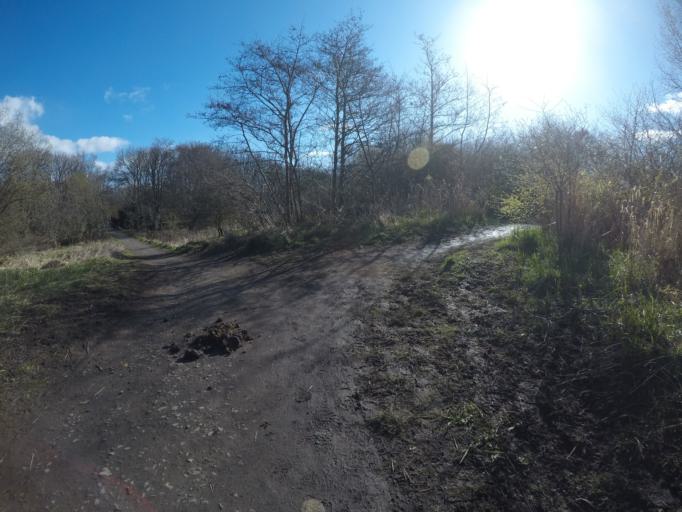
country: GB
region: Scotland
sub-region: North Ayrshire
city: Irvine
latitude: 55.6469
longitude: -4.6602
